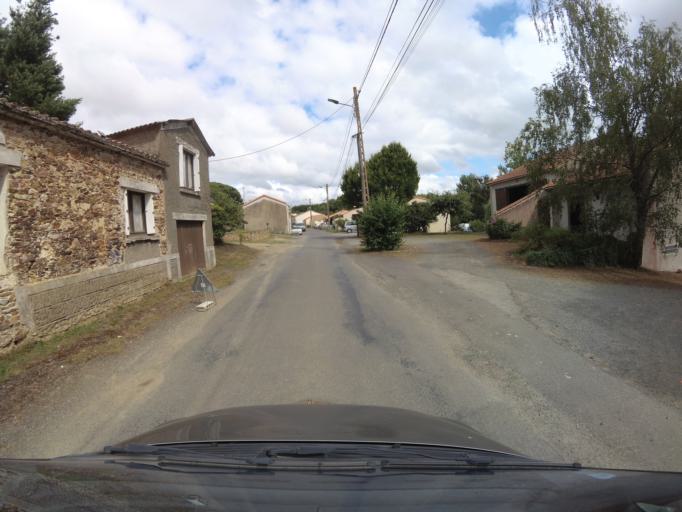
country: FR
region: Pays de la Loire
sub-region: Departement de la Loire-Atlantique
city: La Limouziniere
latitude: 47.0165
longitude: -1.5630
